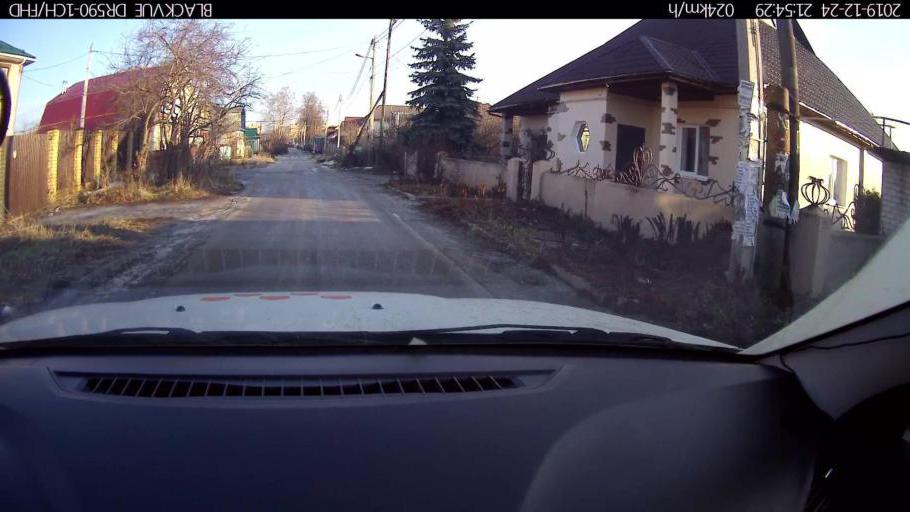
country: RU
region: Nizjnij Novgorod
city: Burevestnik
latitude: 56.2175
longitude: 43.8458
